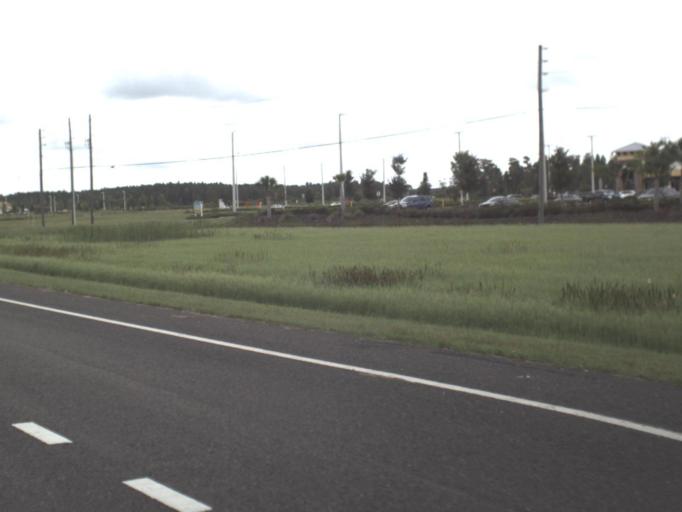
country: US
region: Florida
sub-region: Hillsborough County
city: Cheval
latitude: 28.1933
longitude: -82.5030
